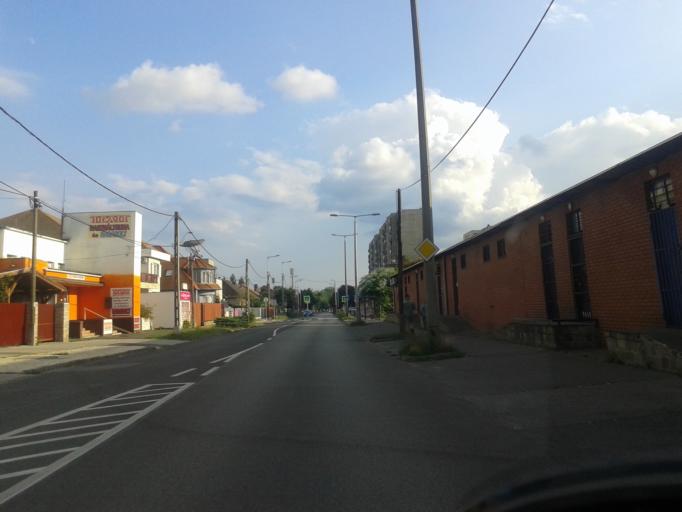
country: HU
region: Budapest
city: Budapest XXI. keruelet
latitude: 47.4248
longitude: 19.0720
